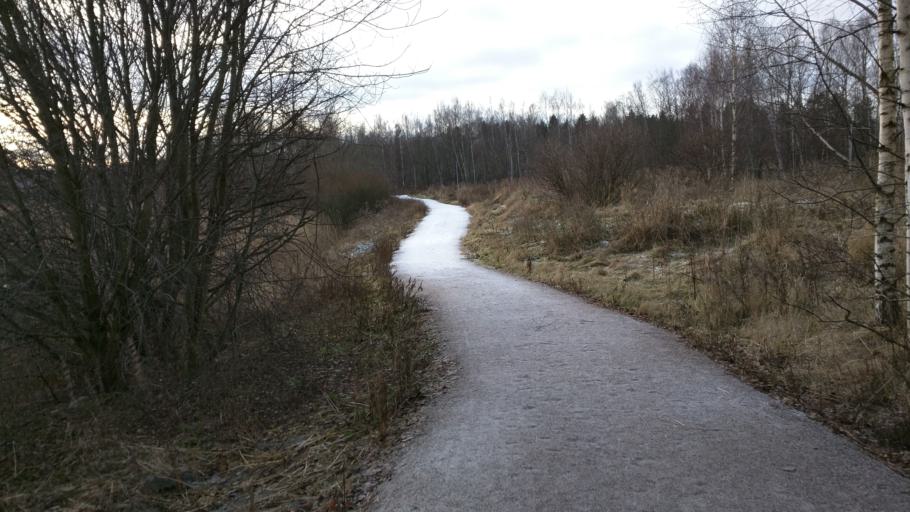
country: FI
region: Uusimaa
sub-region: Helsinki
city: Koukkuniemi
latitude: 60.1533
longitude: 24.7148
